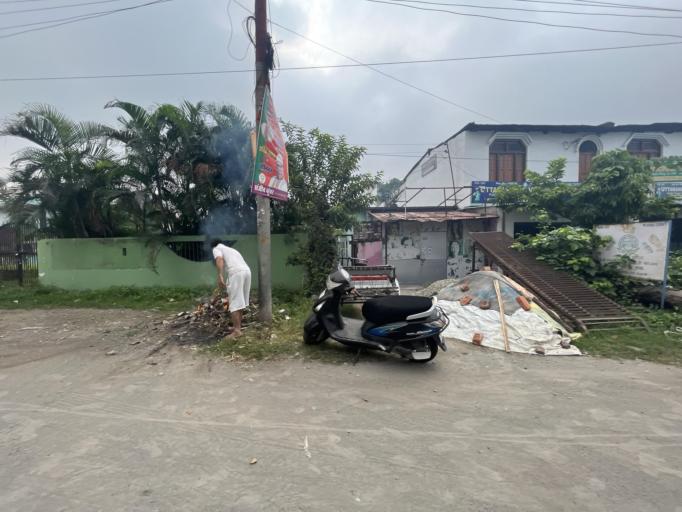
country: IN
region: Uttarakhand
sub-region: Naini Tal
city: Haldwani
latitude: 29.1947
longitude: 79.5104
